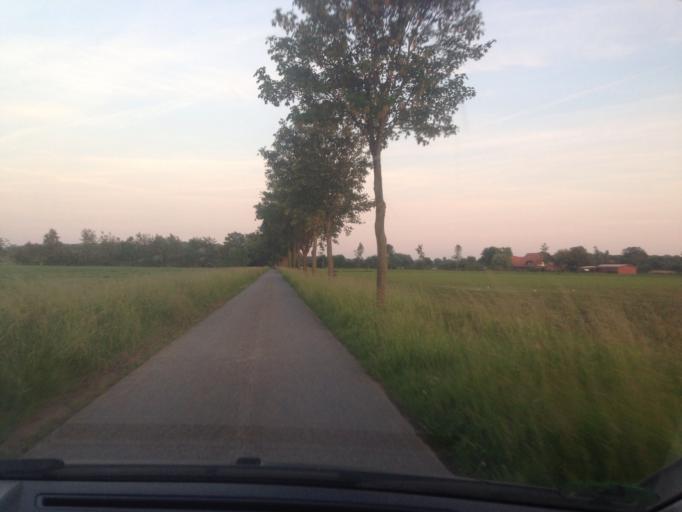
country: DE
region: North Rhine-Westphalia
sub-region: Regierungsbezirk Munster
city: Greven
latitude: 52.0280
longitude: 7.5788
